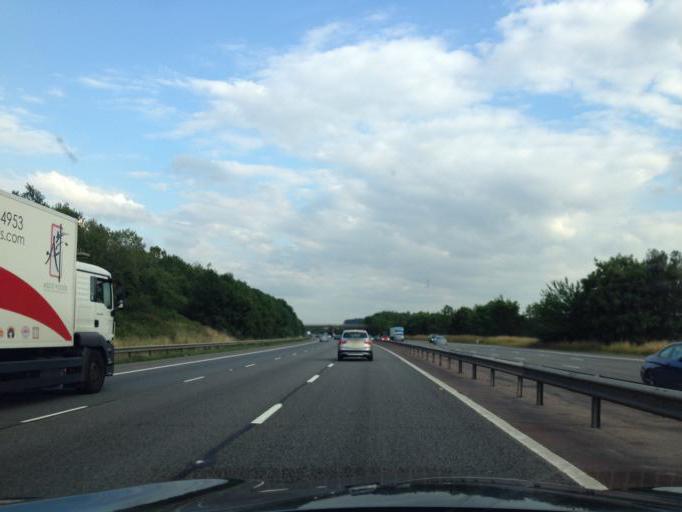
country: GB
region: England
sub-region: Oxfordshire
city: Hanwell
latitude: 52.1435
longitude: -1.4135
